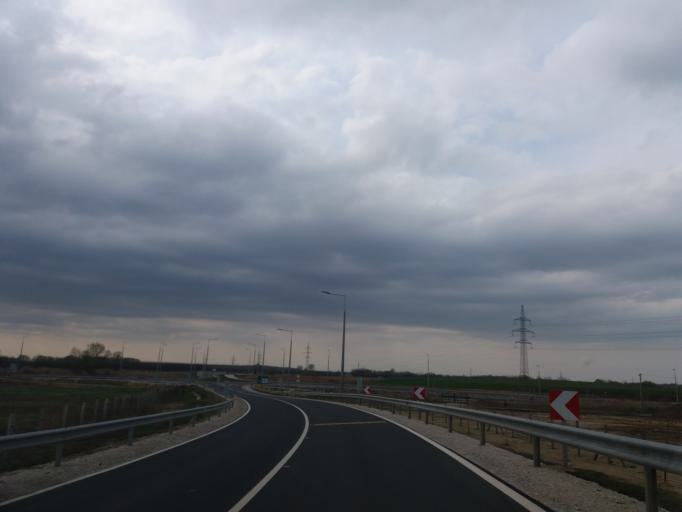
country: HU
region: Szabolcs-Szatmar-Bereg
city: Kisvarda
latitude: 48.2022
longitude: 22.0693
